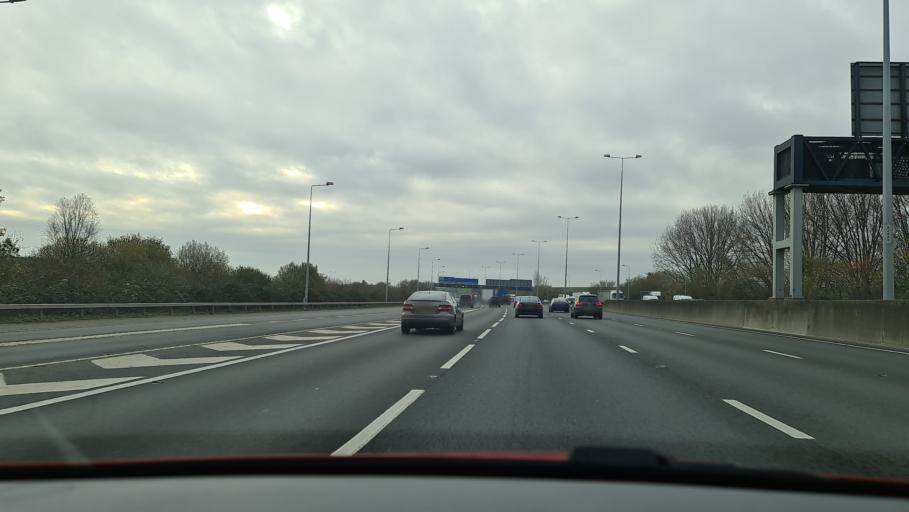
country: GB
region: England
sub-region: Surrey
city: Colnbrook
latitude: 51.4622
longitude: -0.5124
